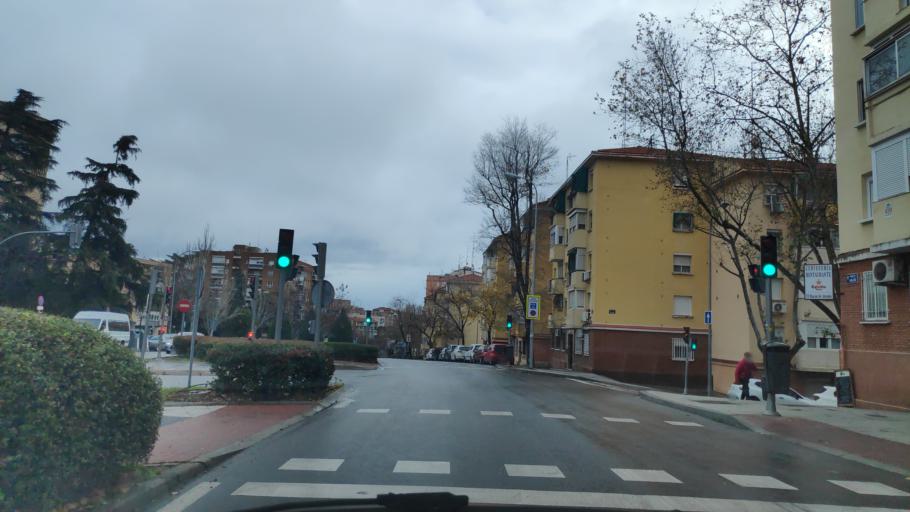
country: ES
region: Madrid
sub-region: Provincia de Madrid
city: Hortaleza
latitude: 40.4720
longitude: -3.6533
